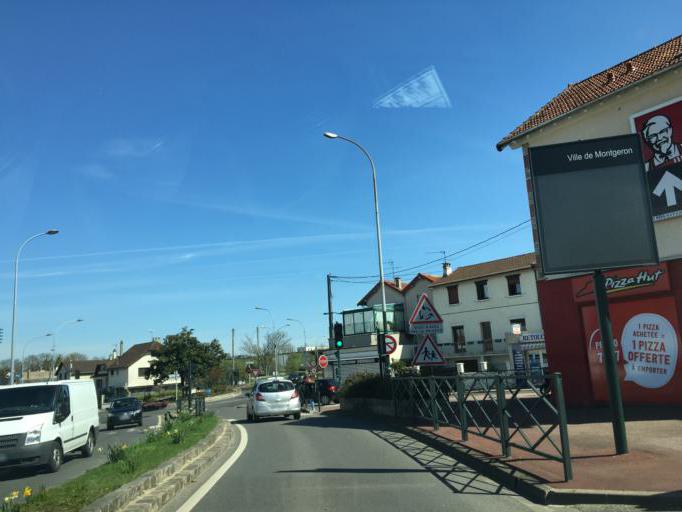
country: FR
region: Ile-de-France
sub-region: Departement de l'Essonne
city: Montgeron
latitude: 48.7062
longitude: 2.4404
